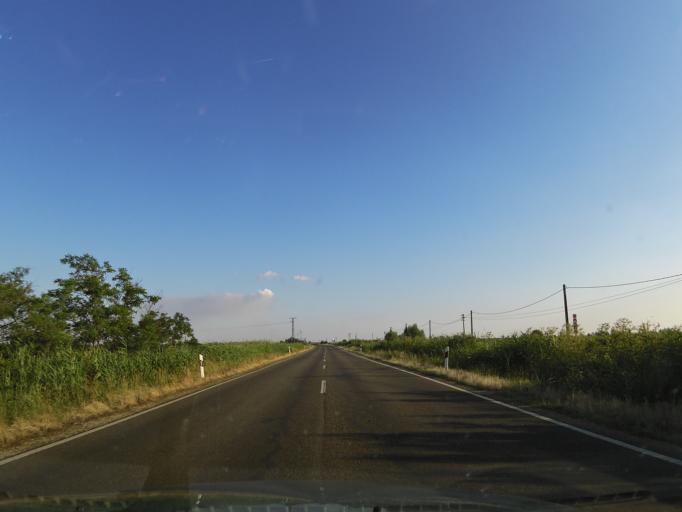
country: HU
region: Jasz-Nagykun-Szolnok
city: Tiszafoldvar
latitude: 46.9393
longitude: 20.2686
